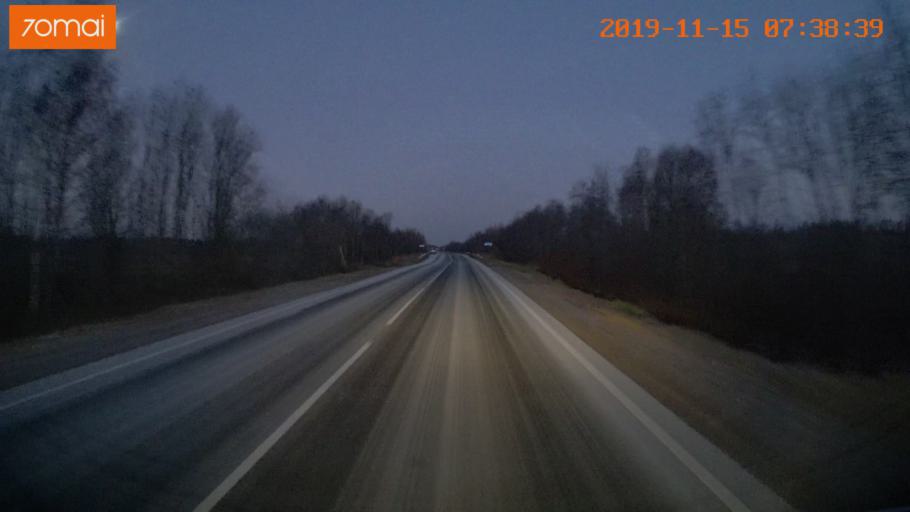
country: RU
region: Vologda
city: Sheksna
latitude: 58.7591
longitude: 38.3973
